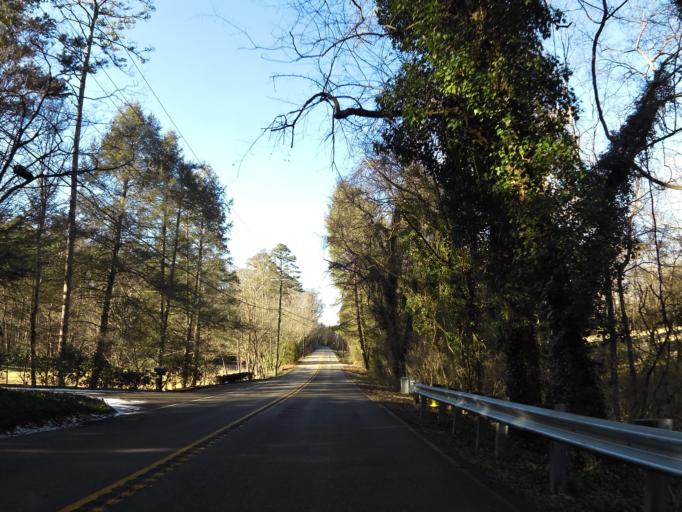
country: US
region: Tennessee
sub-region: Knox County
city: Knoxville
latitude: 35.9120
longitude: -83.9859
